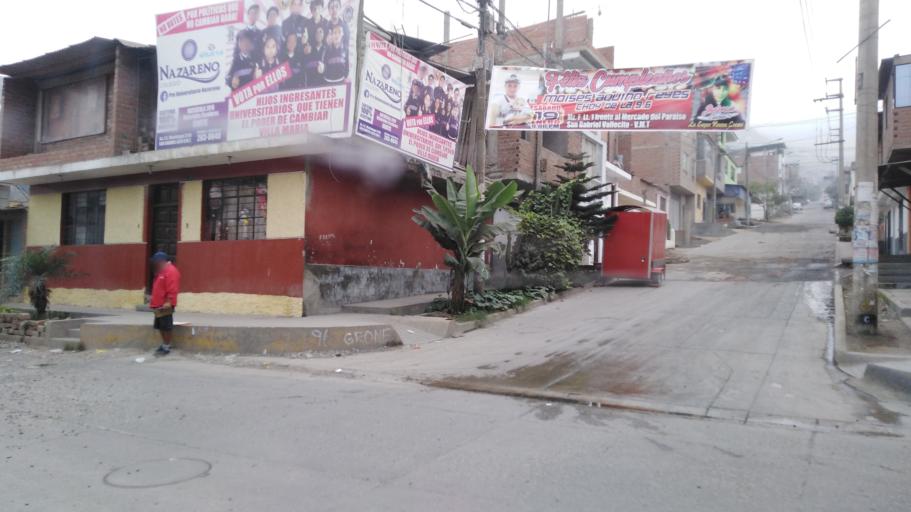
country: PE
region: Lima
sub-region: Lima
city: La Molina
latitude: -12.1421
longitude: -76.9393
